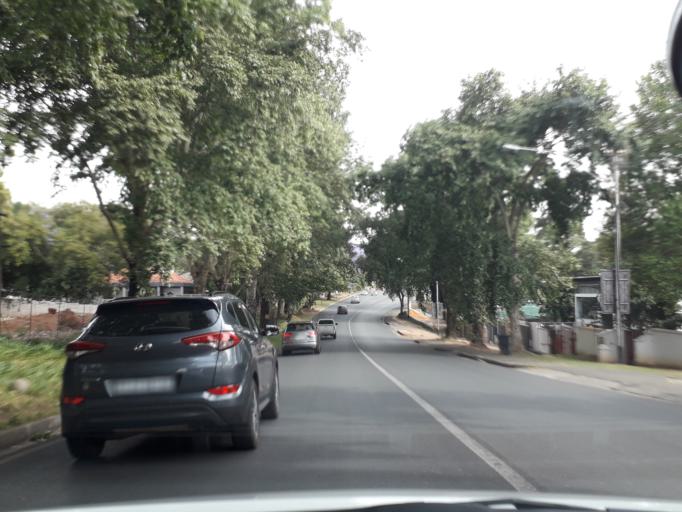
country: ZA
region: Gauteng
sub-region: City of Johannesburg Metropolitan Municipality
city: Johannesburg
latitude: -26.1404
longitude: 28.0352
